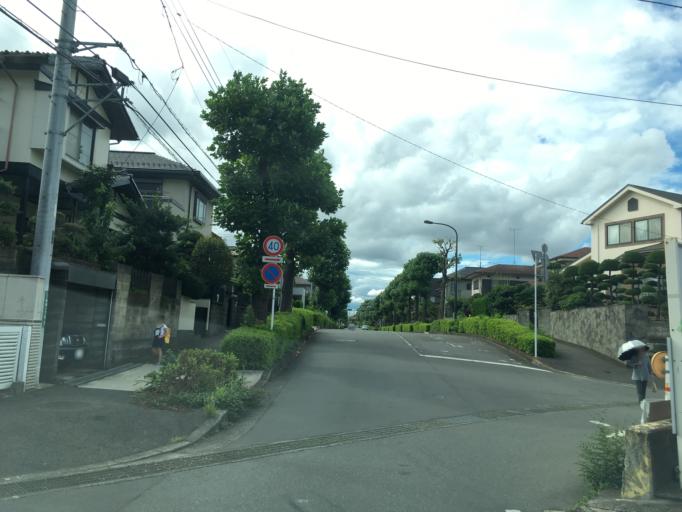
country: JP
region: Kanagawa
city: Minami-rinkan
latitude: 35.5068
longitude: 139.4700
